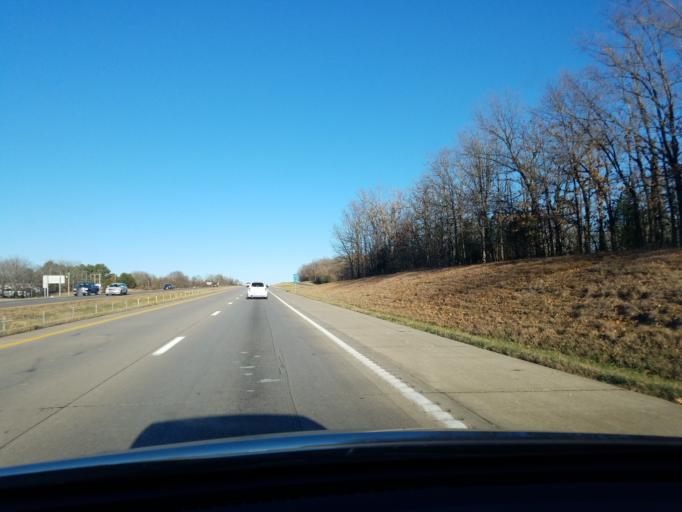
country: US
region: Missouri
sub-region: Crawford County
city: Cuba
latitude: 38.1114
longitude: -91.3318
